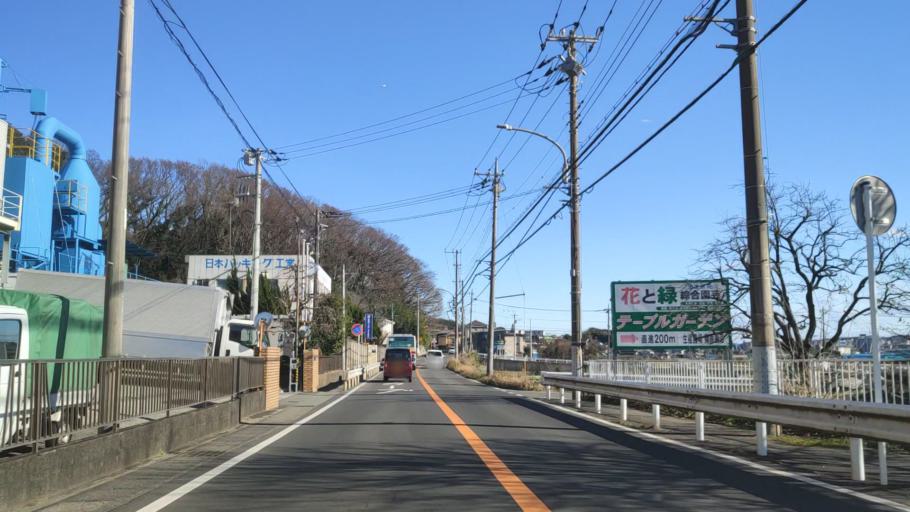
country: JP
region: Tokyo
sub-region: Machida-shi
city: Machida
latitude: 35.5272
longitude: 139.5273
